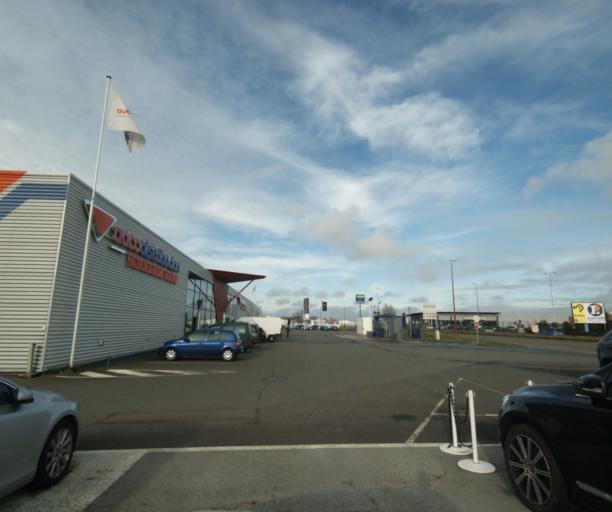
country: FR
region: Pays de la Loire
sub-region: Departement de la Sarthe
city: Allonnes
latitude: 47.9745
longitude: 0.1730
